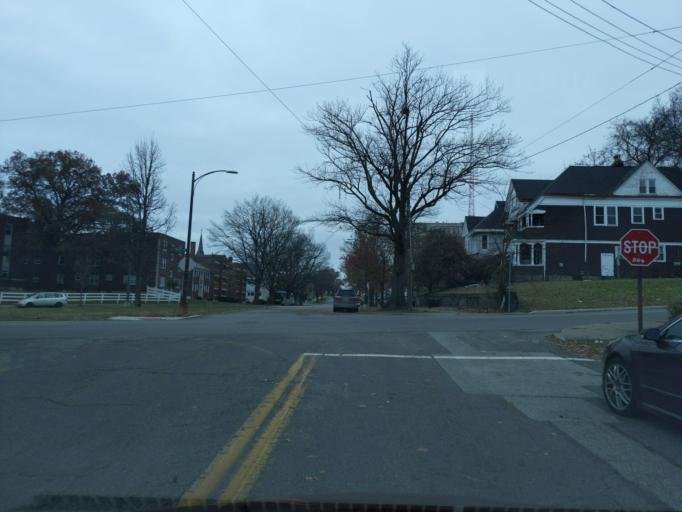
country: US
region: Kentucky
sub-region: Campbell County
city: Dayton
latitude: 39.1290
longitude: -84.4842
